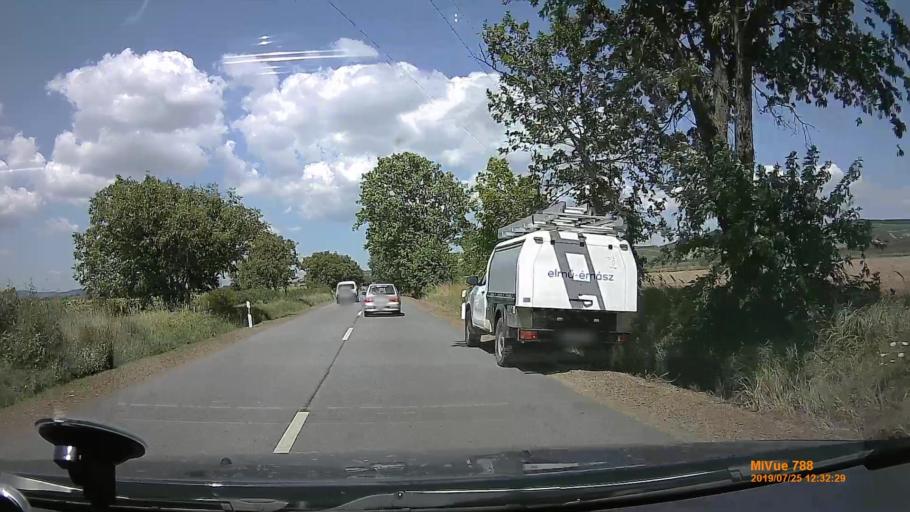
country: HU
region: Borsod-Abauj-Zemplen
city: Tarcal
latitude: 48.1520
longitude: 21.3157
